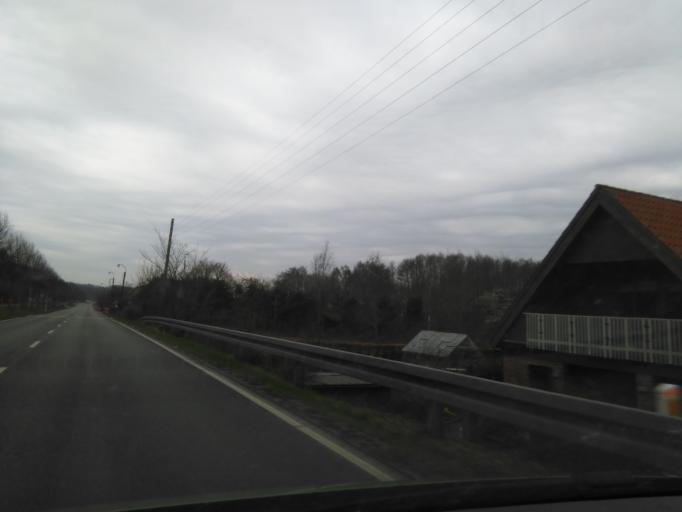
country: DK
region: North Denmark
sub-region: Mariagerfjord Kommune
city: Hadsund
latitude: 56.7063
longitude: 10.1166
